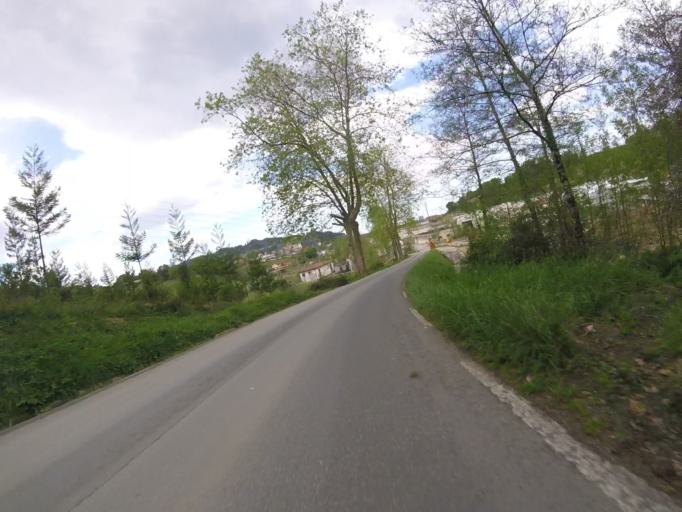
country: ES
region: Basque Country
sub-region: Provincia de Guipuzcoa
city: Zarautz
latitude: 43.2723
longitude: -2.1688
